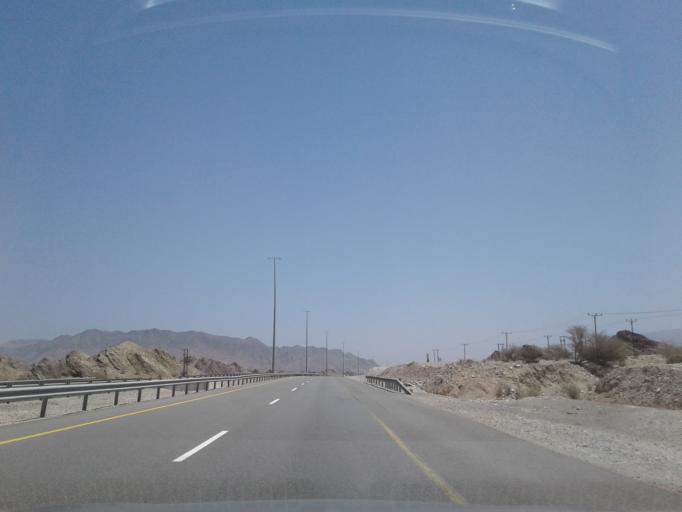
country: OM
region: Muhafazat Masqat
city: Muscat
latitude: 23.3464
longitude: 58.6936
